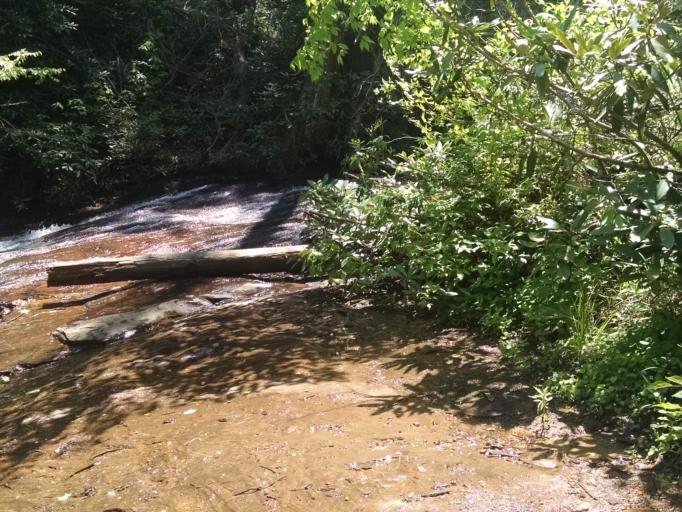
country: US
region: Georgia
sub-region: Union County
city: Blairsville
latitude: 34.7530
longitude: -83.8954
